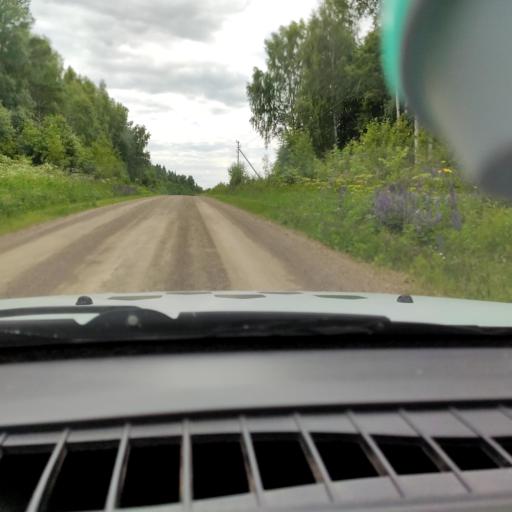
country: RU
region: Perm
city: Suksun
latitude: 57.1959
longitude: 57.5894
